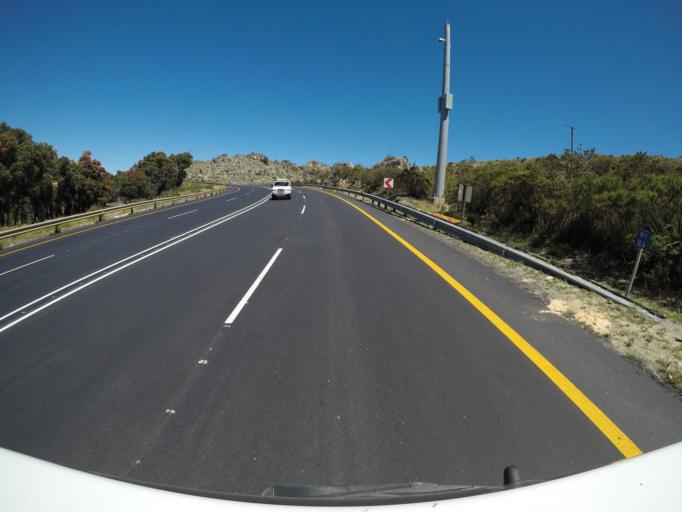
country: ZA
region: Western Cape
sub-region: Overberg District Municipality
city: Grabouw
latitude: -34.1500
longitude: 18.9336
